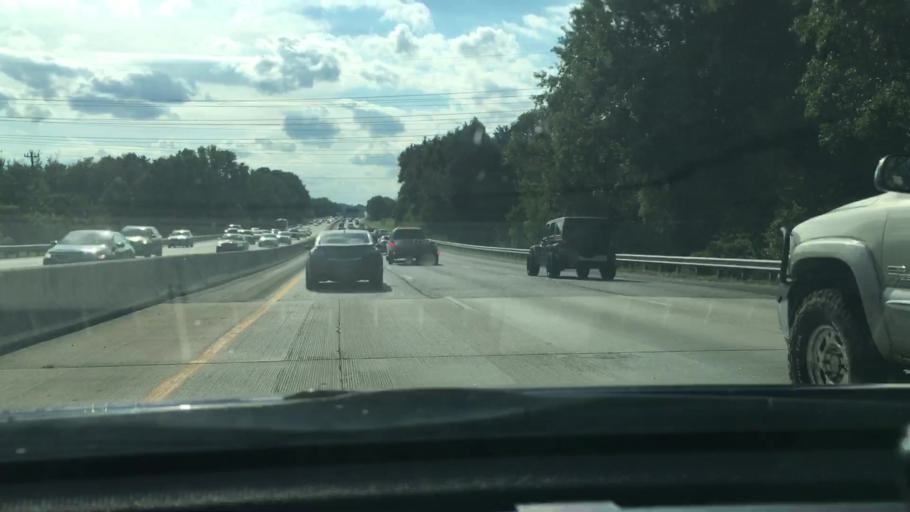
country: US
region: South Carolina
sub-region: Richland County
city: Columbia
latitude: 34.0536
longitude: -81.0605
